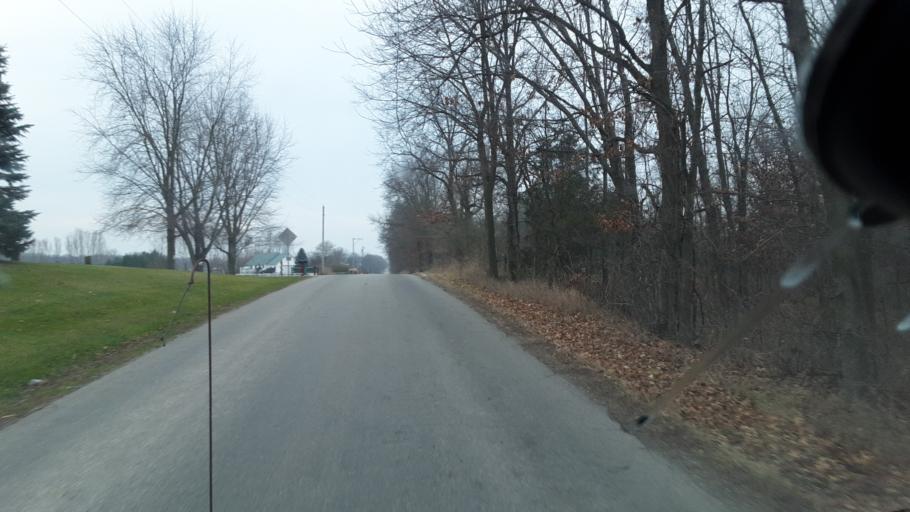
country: US
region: Michigan
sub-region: Saint Joseph County
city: White Pigeon
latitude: 41.7253
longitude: -85.6209
